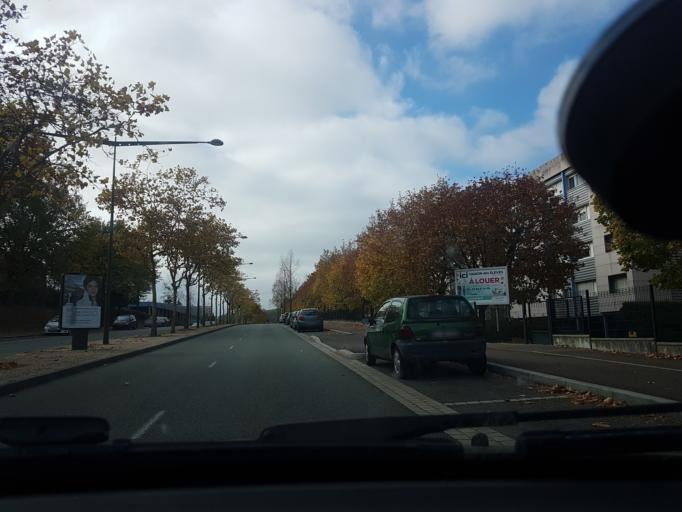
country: FR
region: Franche-Comte
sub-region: Territoire de Belfort
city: Cravanche
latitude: 47.6409
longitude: 6.8467
